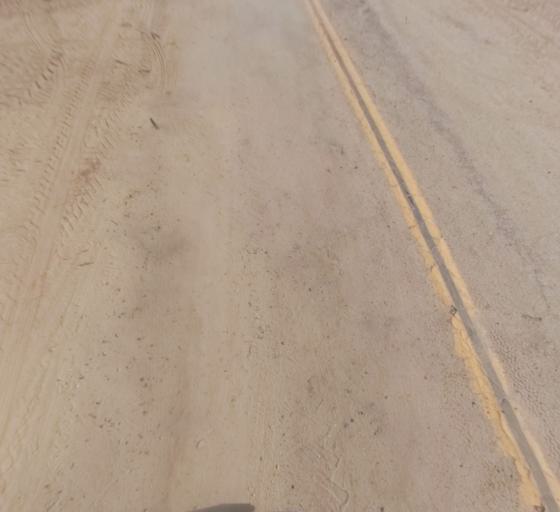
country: US
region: California
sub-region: Fresno County
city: Biola
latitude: 36.8226
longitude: -120.0653
